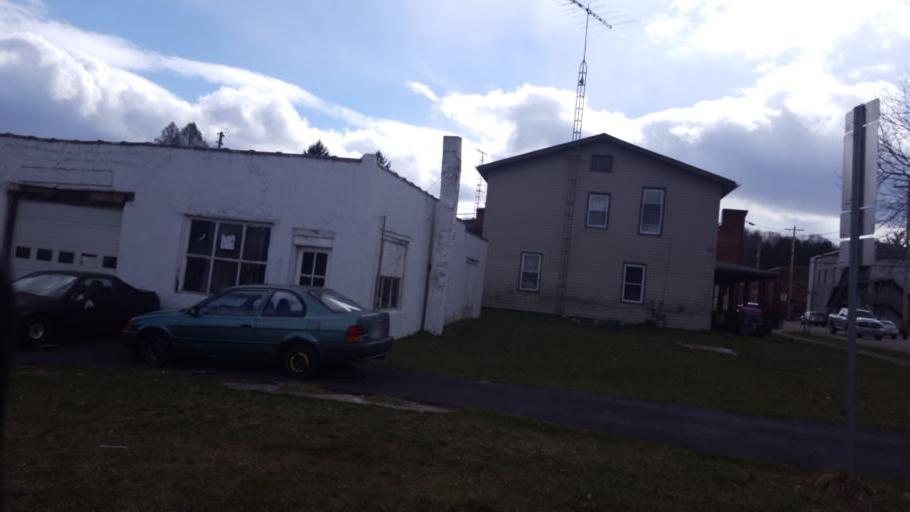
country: US
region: Ohio
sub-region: Richland County
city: Lincoln Heights
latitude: 40.7047
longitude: -82.4180
